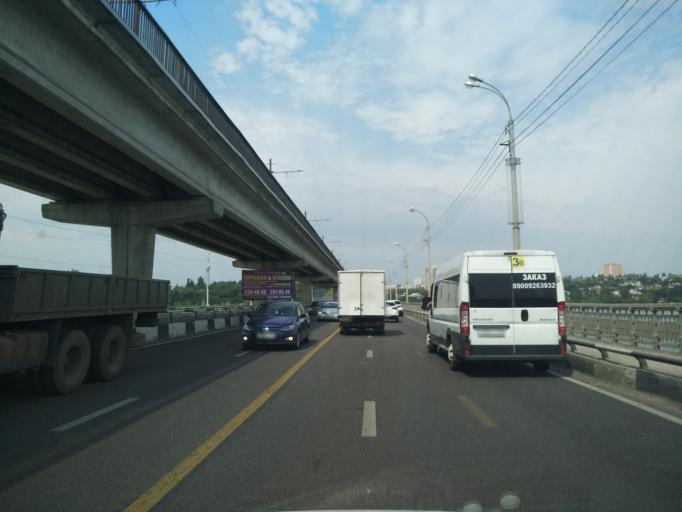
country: RU
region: Voronezj
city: Voronezh
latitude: 51.6911
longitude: 39.2433
